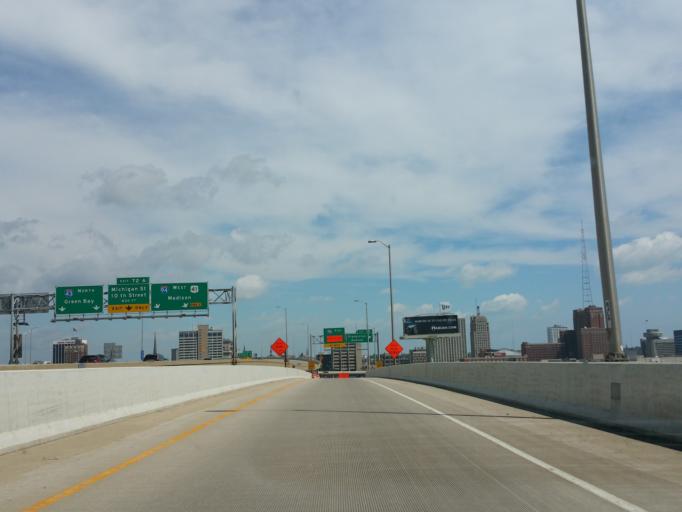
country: US
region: Wisconsin
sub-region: Milwaukee County
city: Milwaukee
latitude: 43.0305
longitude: -87.9224
